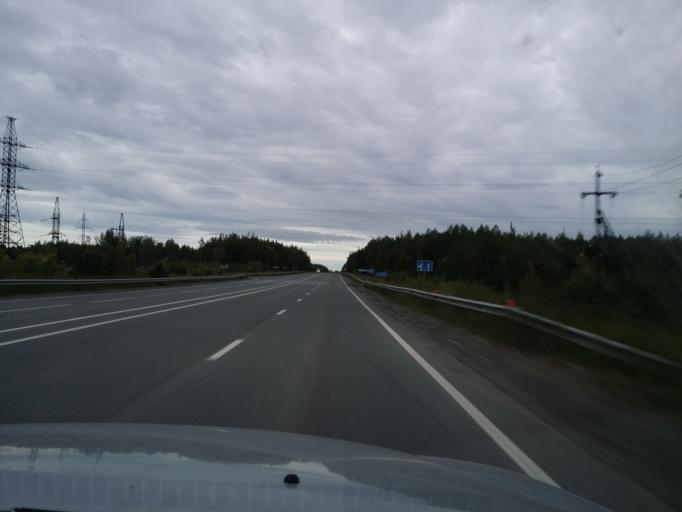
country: RU
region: Khanty-Mansiyskiy Avtonomnyy Okrug
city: Izluchinsk
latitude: 61.0467
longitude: 76.9005
